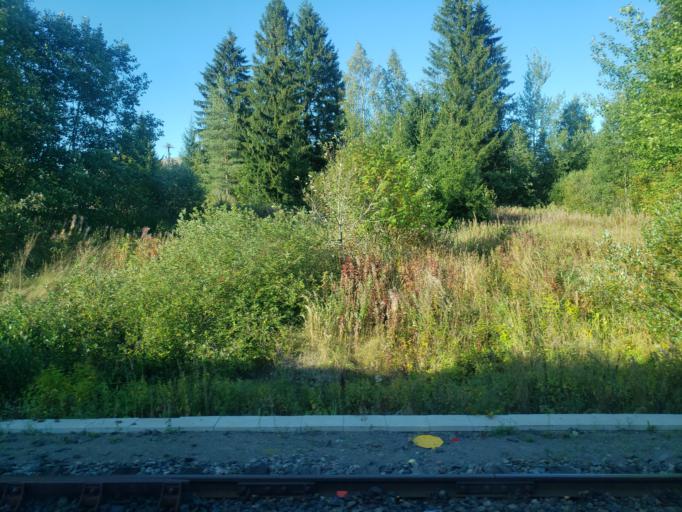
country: FI
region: South Karelia
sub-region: Lappeenranta
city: Lappeenranta
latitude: 60.8681
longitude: 28.2871
